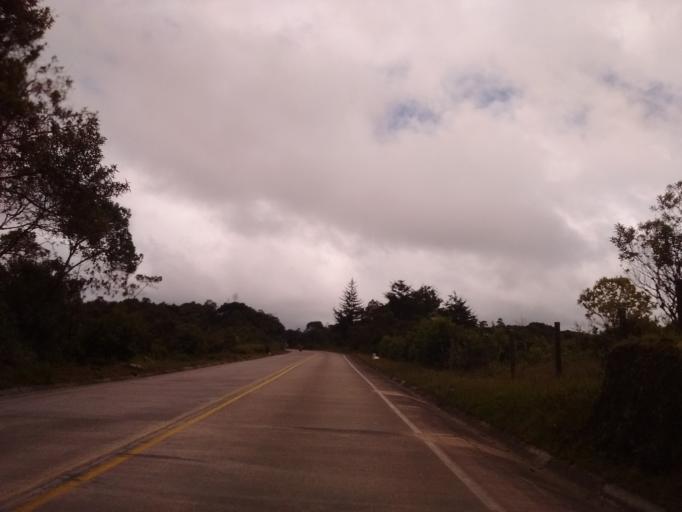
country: CO
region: Huila
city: Isnos
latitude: 2.0534
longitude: -76.3206
